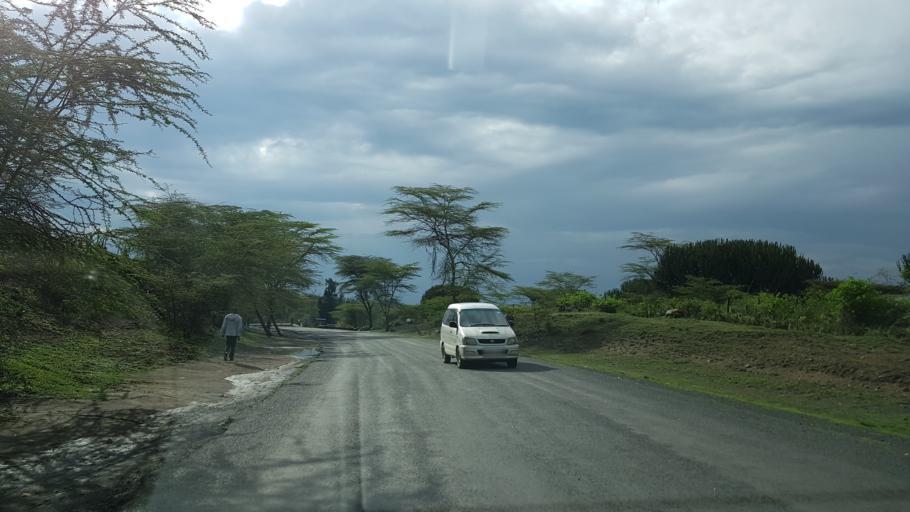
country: KE
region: Nakuru
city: Naivasha
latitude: -0.8280
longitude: 36.3357
